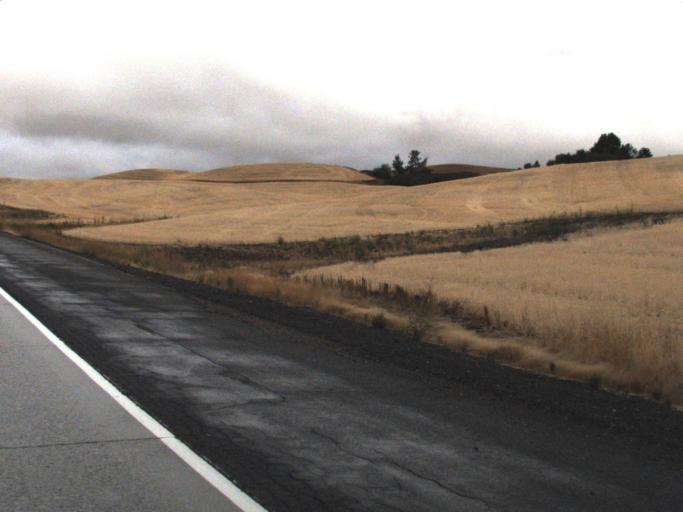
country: US
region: Washington
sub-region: Whitman County
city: Colfax
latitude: 47.1016
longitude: -117.3789
